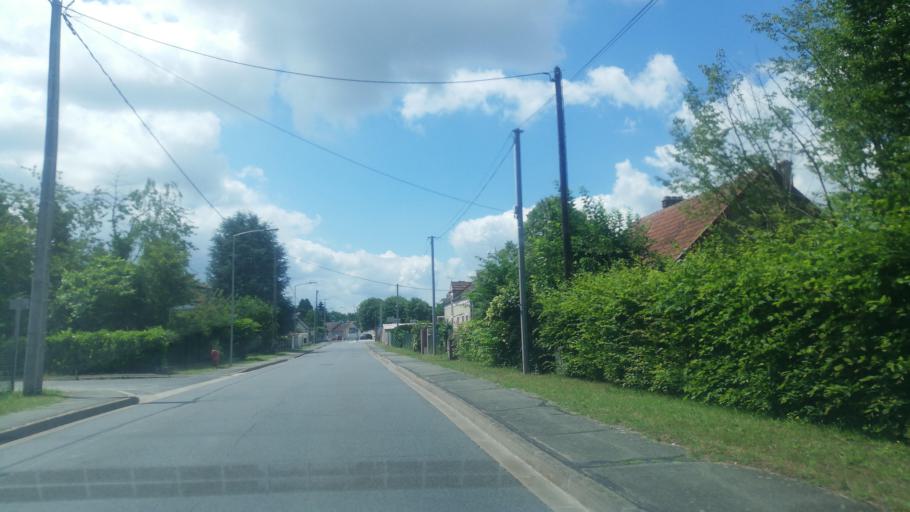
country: FR
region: Centre
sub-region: Departement du Loir-et-Cher
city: Contres
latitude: 47.4238
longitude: 1.4296
